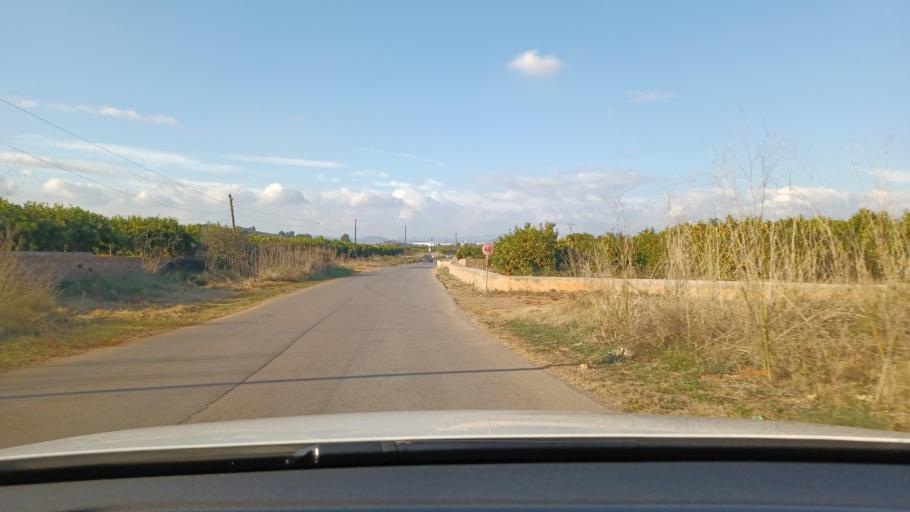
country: ES
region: Valencia
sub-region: Provincia de Castello
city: Betxi
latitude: 39.9361
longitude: -0.2071
